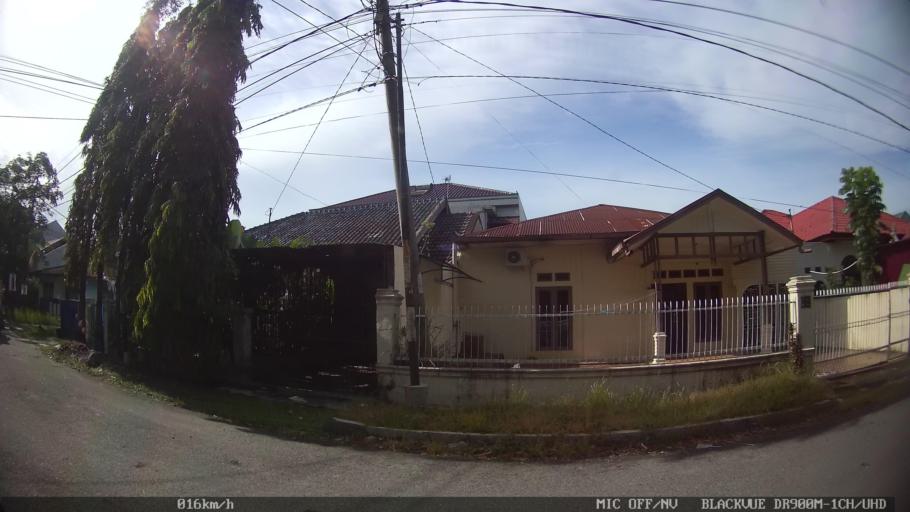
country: ID
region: North Sumatra
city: Medan
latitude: 3.6118
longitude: 98.6598
